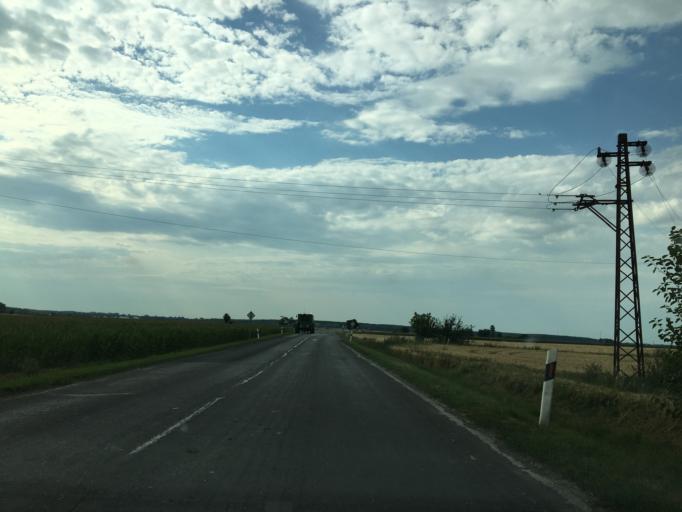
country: HU
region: Bacs-Kiskun
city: Dusnok
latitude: 46.4182
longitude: 18.9447
